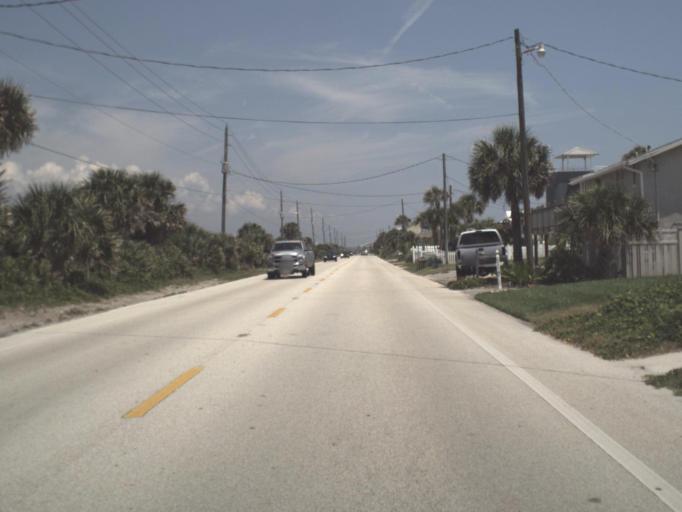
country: US
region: Florida
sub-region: Saint Johns County
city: Villano Beach
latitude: 29.9269
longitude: -81.2957
